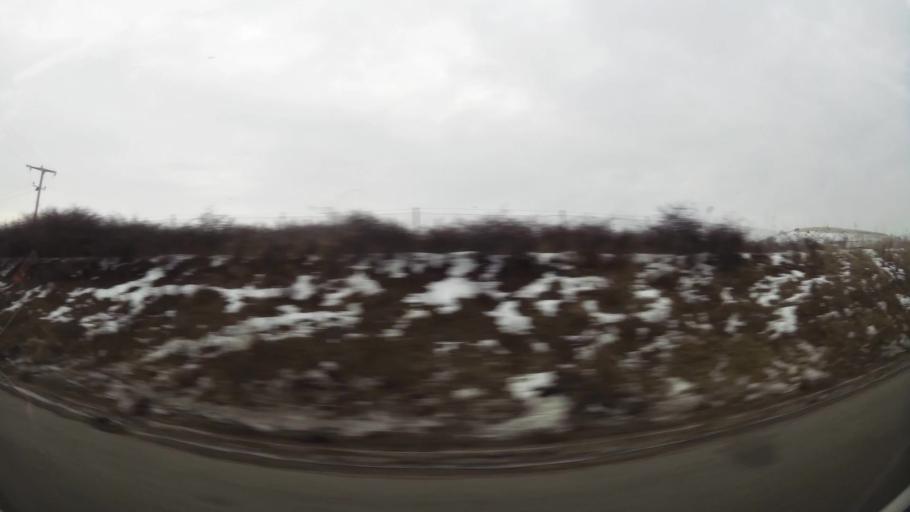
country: MK
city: Kondovo
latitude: 42.0269
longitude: 21.3299
